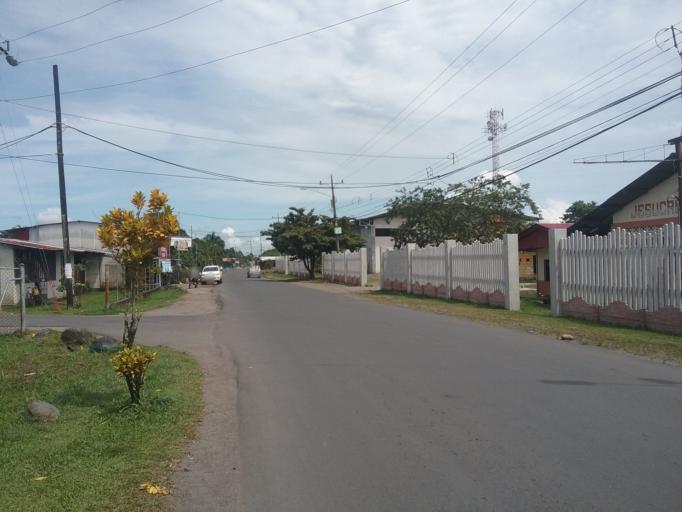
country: CR
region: Limon
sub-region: Canton de Pococi
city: Roxana
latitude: 10.3230
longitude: -83.8860
